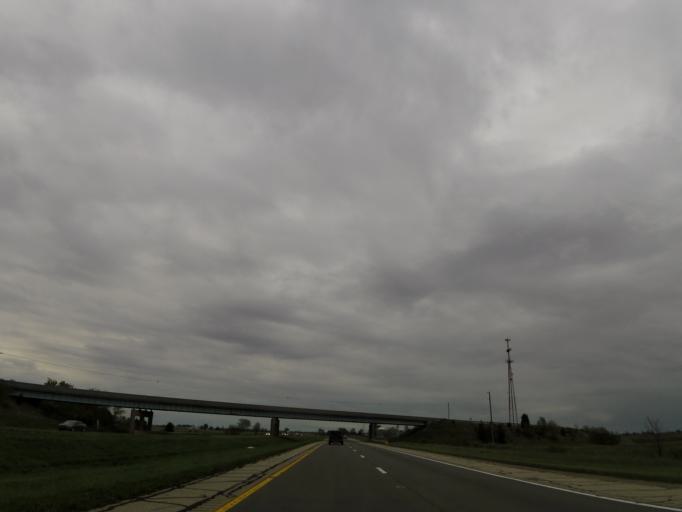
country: US
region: Ohio
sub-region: Madison County
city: Bethel
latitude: 39.7292
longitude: -83.3745
